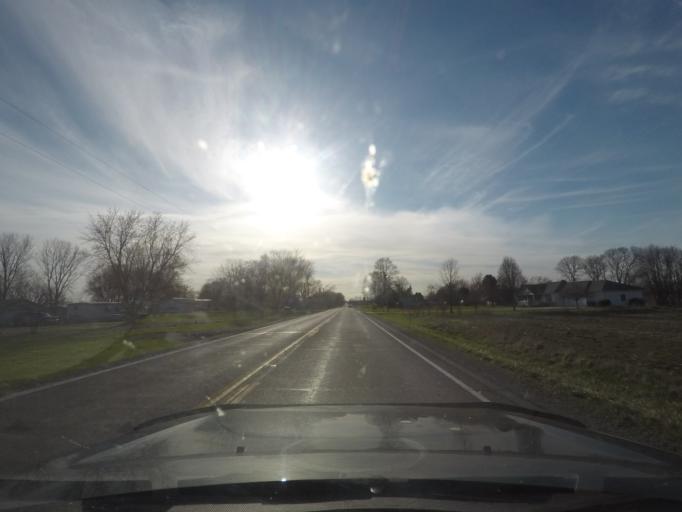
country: US
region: Indiana
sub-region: Saint Joseph County
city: North Liberty
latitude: 41.4486
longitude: -86.3749
